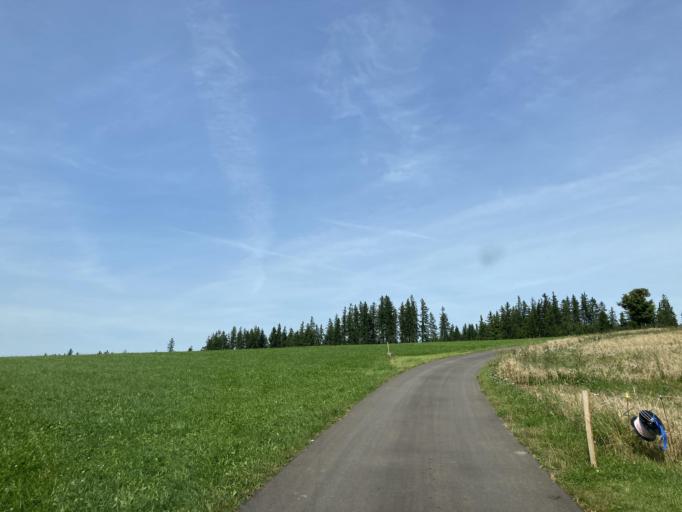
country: DE
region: Baden-Wuerttemberg
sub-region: Freiburg Region
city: Triberg im Schwarzwald
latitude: 48.1168
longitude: 8.2822
